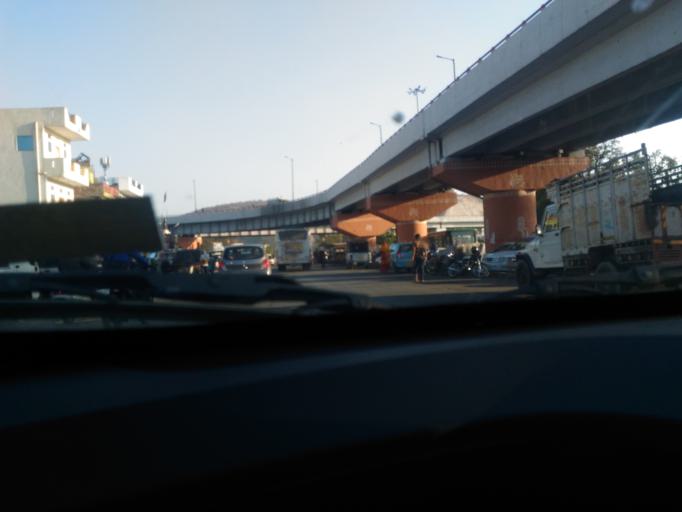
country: IN
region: Rajasthan
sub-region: Jaipur
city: Jaipur
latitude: 26.9050
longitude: 75.8437
